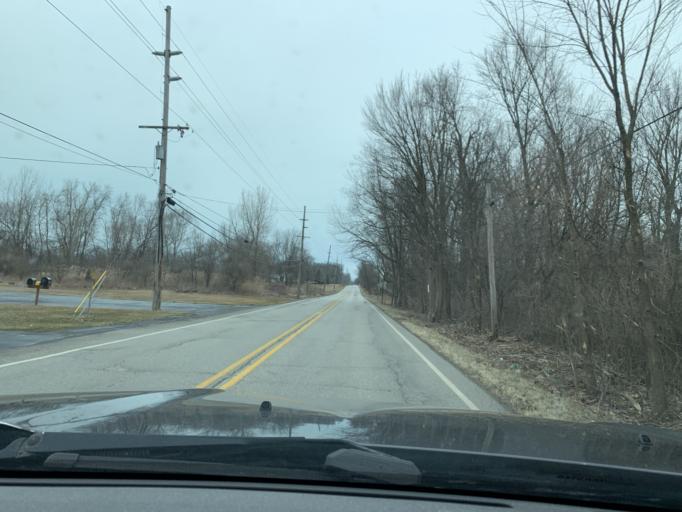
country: US
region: Indiana
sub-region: Porter County
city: Chesterton
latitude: 41.5812
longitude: -87.0666
